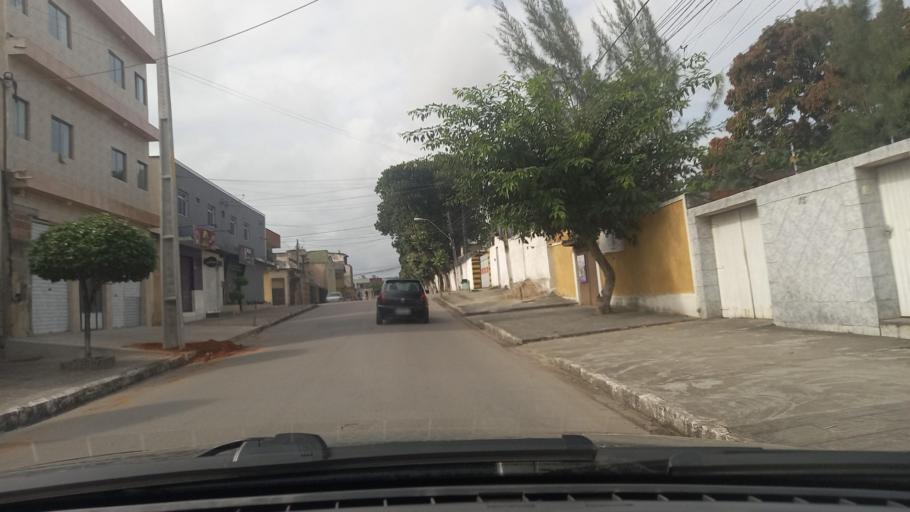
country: BR
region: Pernambuco
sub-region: Vitoria De Santo Antao
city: Vitoria de Santo Antao
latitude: -8.1115
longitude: -35.2975
